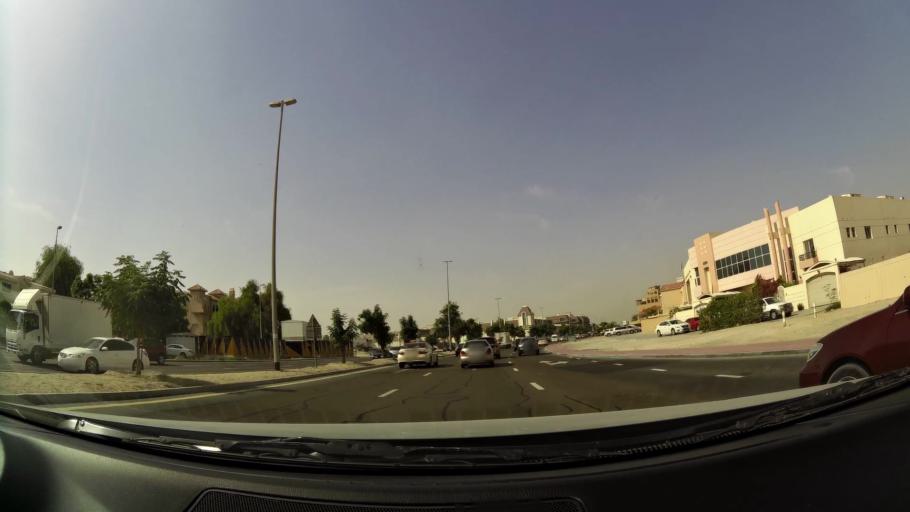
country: AE
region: Ash Shariqah
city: Sharjah
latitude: 25.2281
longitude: 55.4250
